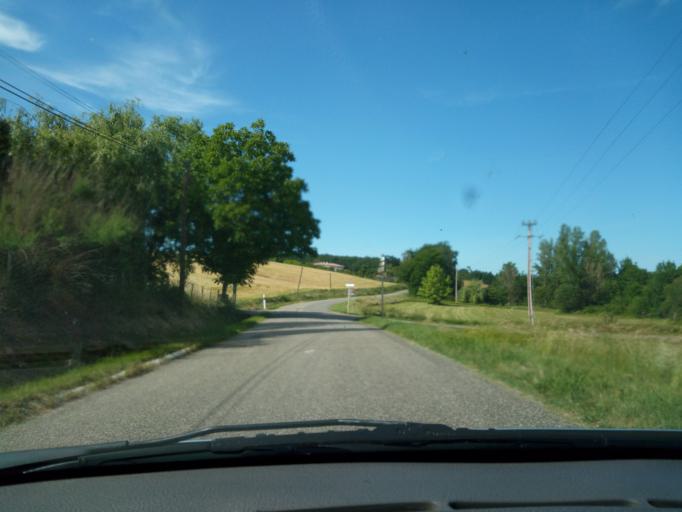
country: FR
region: Midi-Pyrenees
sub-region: Departement du Tarn-et-Garonne
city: Molieres
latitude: 44.2102
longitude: 1.3120
